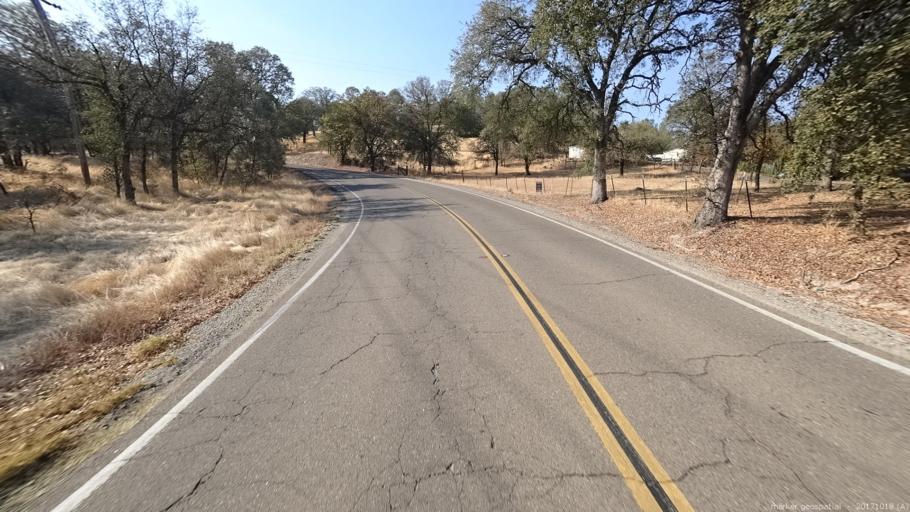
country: US
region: California
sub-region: Shasta County
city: Palo Cedro
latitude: 40.5639
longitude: -122.2472
